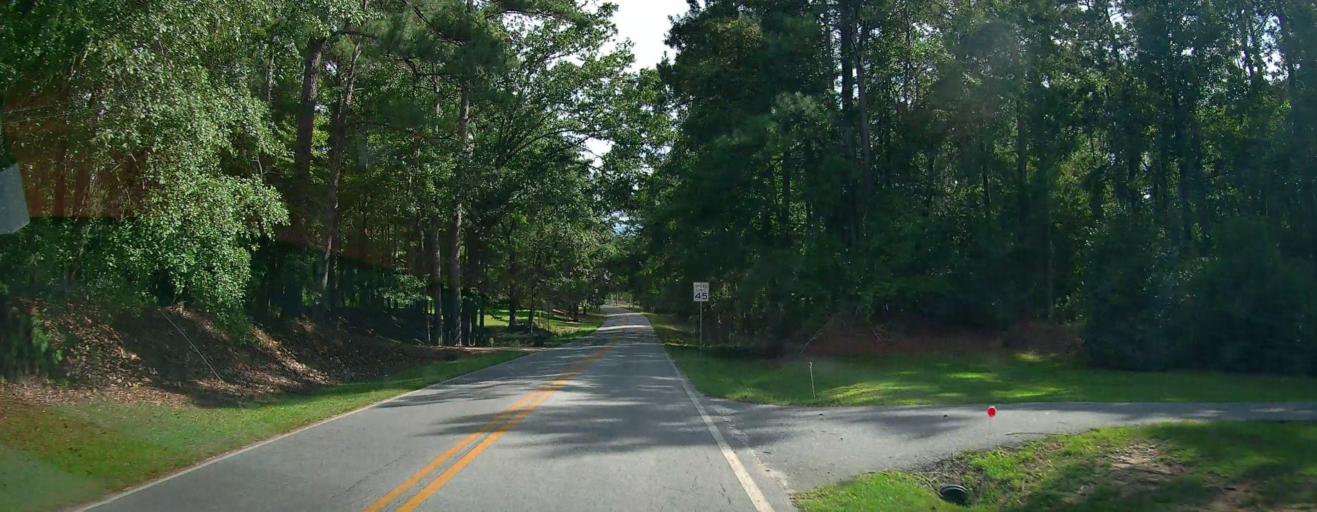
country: US
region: Alabama
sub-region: Lee County
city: Smiths Station
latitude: 32.6067
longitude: -84.9819
